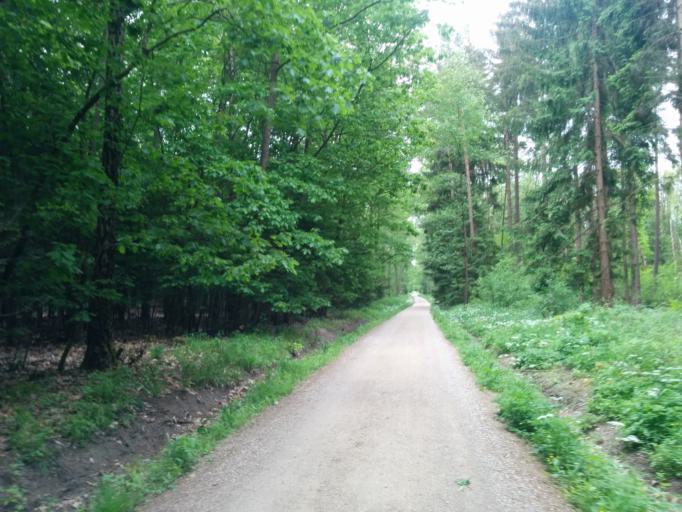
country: DE
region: Bavaria
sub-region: Regierungsbezirk Mittelfranken
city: Kalchreuth
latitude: 49.5338
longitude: 11.0855
